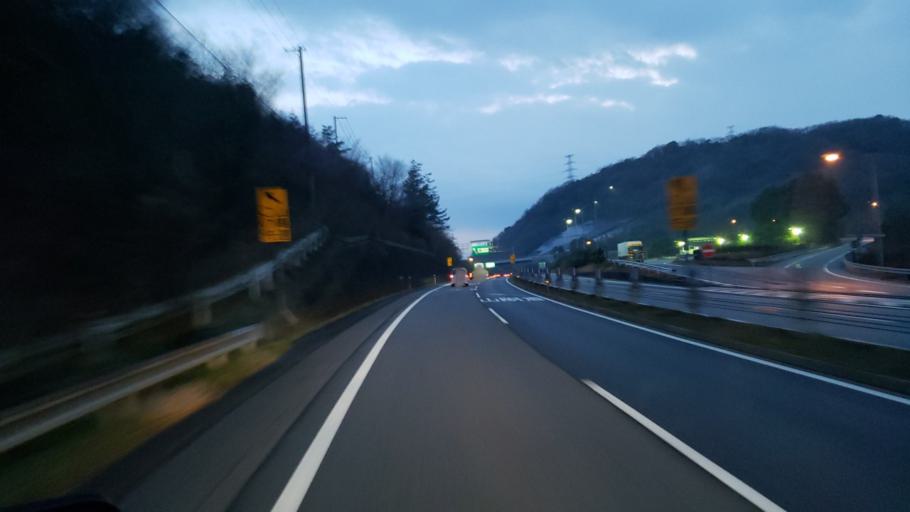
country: JP
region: Hyogo
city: Himeji
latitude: 34.8579
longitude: 134.7399
